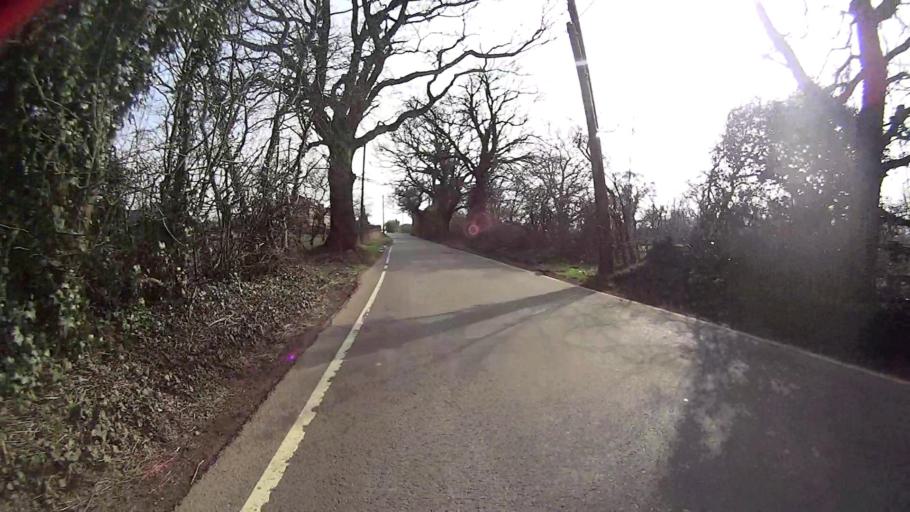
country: GB
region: England
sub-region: Surrey
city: Felbridge
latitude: 51.1886
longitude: -0.0682
